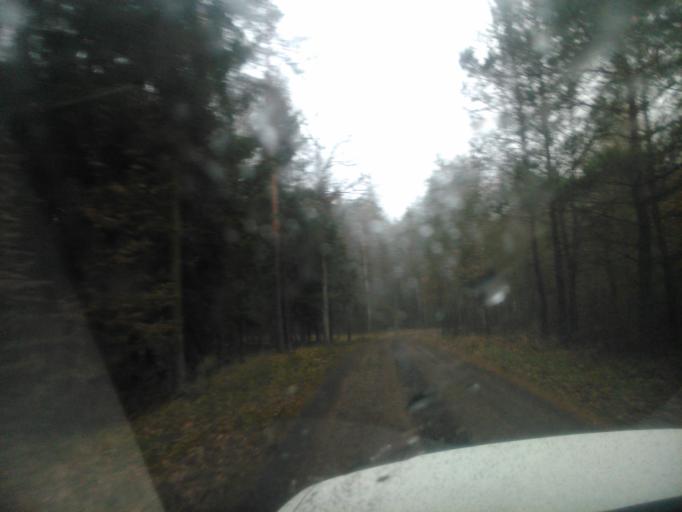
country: PL
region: Kujawsko-Pomorskie
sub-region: Powiat golubsko-dobrzynski
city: Radomin
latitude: 53.1633
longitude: 19.1405
